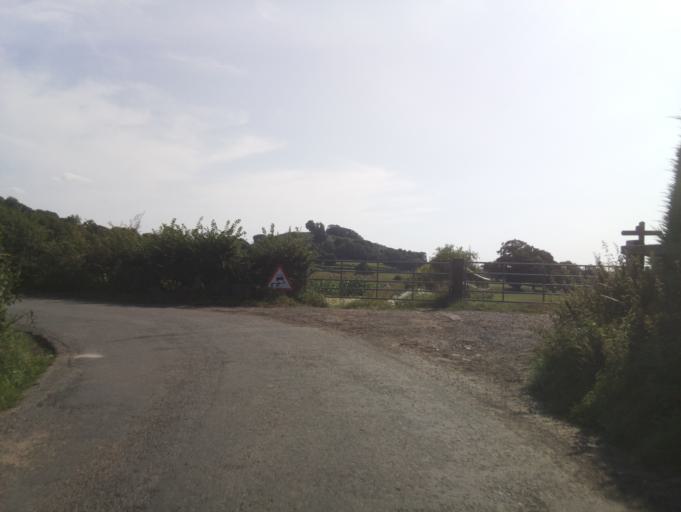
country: GB
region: England
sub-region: Gloucestershire
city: Dursley
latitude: 51.6925
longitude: -2.3192
